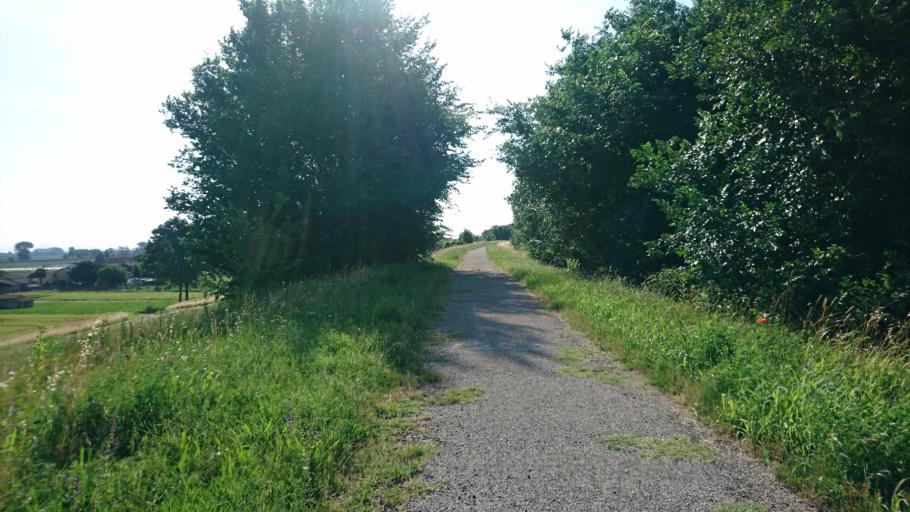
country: IT
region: Veneto
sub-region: Provincia di Verona
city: Villa Bartolomea
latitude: 45.1741
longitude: 11.3375
